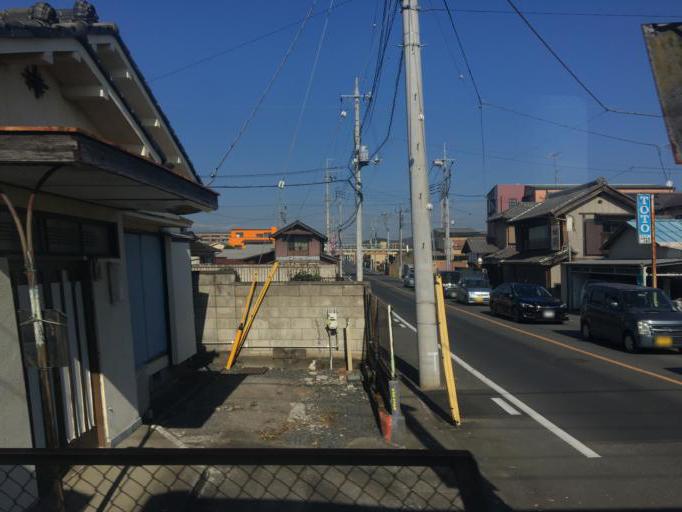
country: JP
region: Tochigi
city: Sano
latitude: 36.3169
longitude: 139.5848
